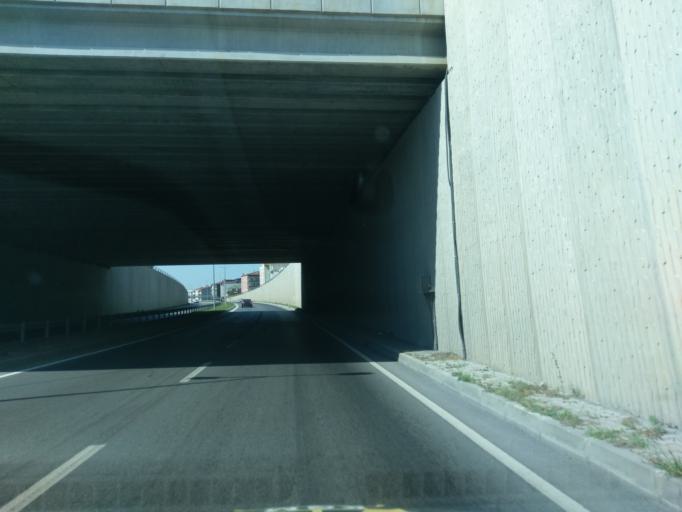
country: TR
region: Samsun
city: Bafra
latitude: 41.5520
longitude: 35.9249
